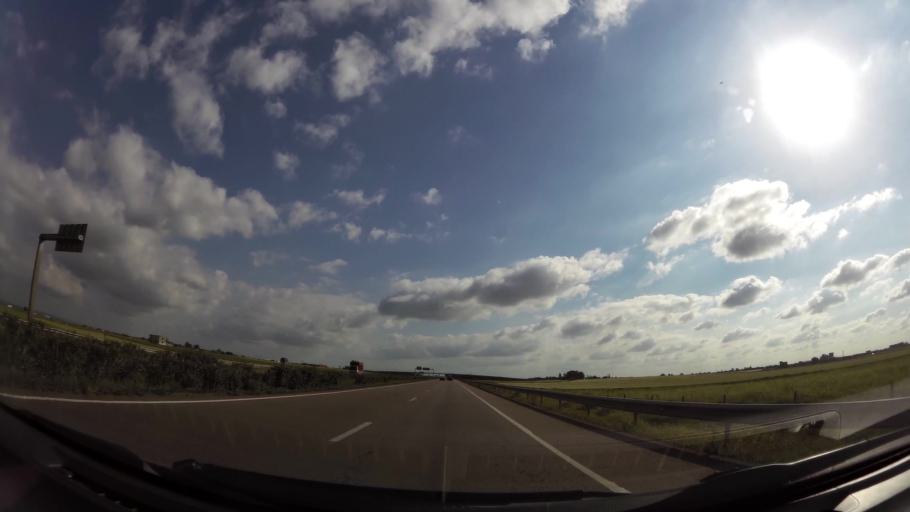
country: MA
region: Chaouia-Ouardigha
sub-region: Settat Province
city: Berrechid
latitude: 33.2435
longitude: -7.5667
